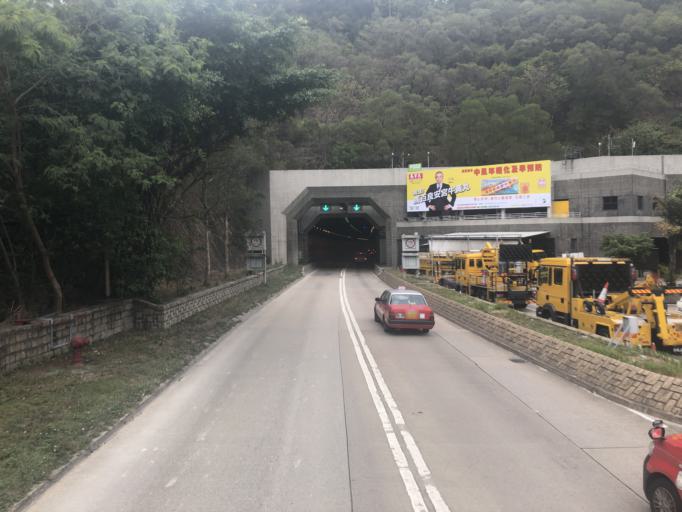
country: HK
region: Kowloon City
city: Kowloon
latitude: 22.3171
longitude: 114.2419
